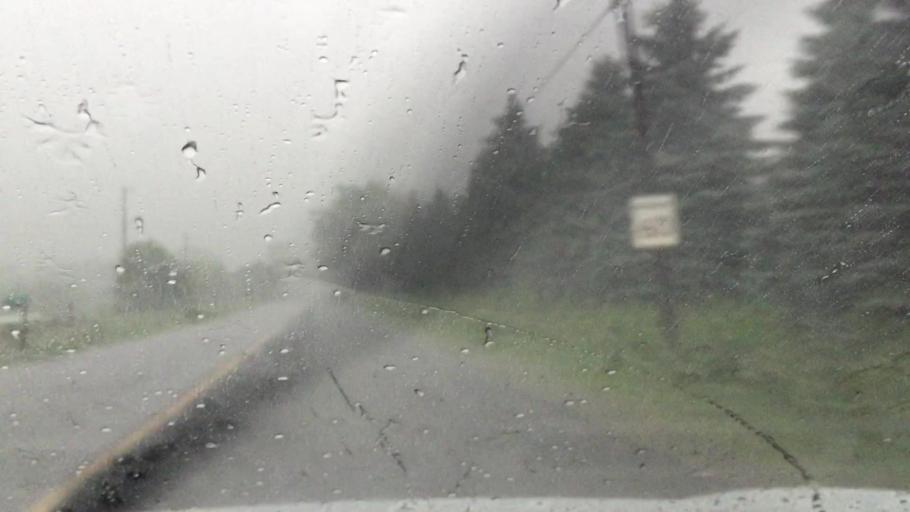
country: CA
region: Ontario
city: Markham
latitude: 43.8543
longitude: -79.2032
